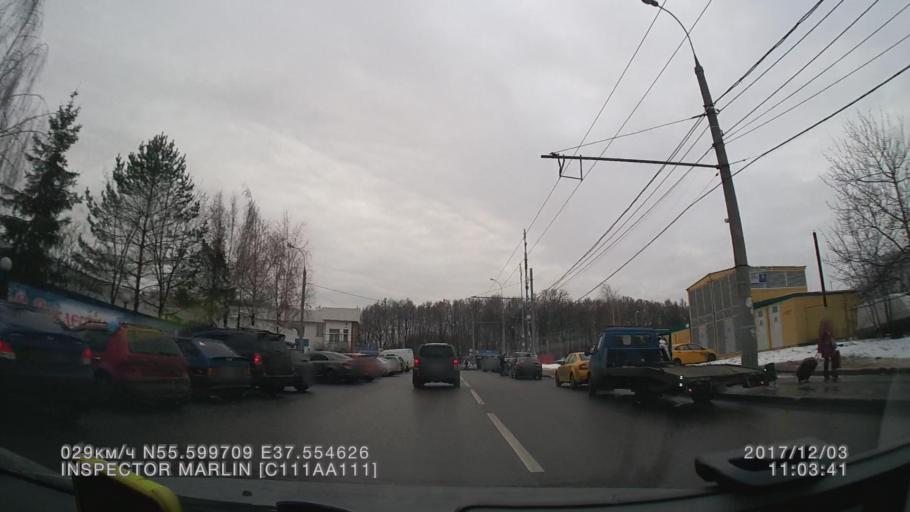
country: RU
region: Moscow
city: Yasenevo
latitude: 55.5997
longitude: 37.5546
